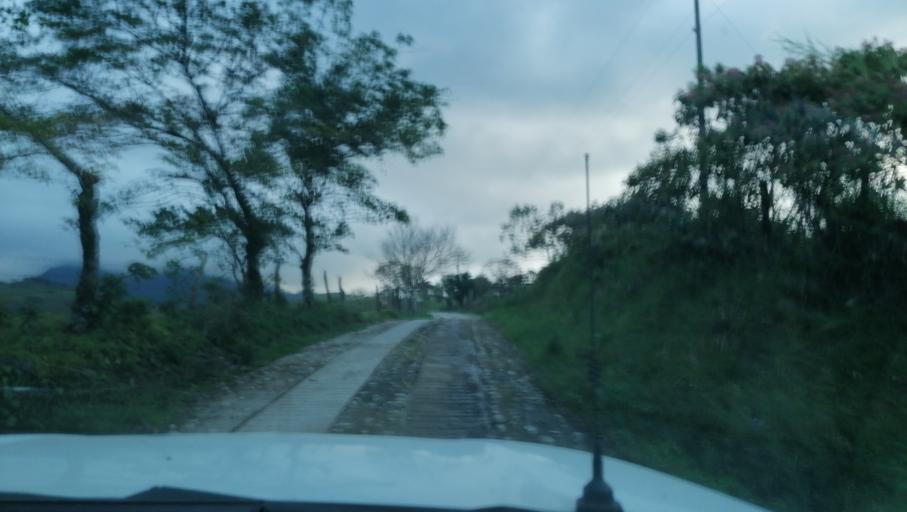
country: MX
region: Chiapas
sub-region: Francisco Leon
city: San Miguel la Sardina
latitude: 17.2959
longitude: -93.2658
